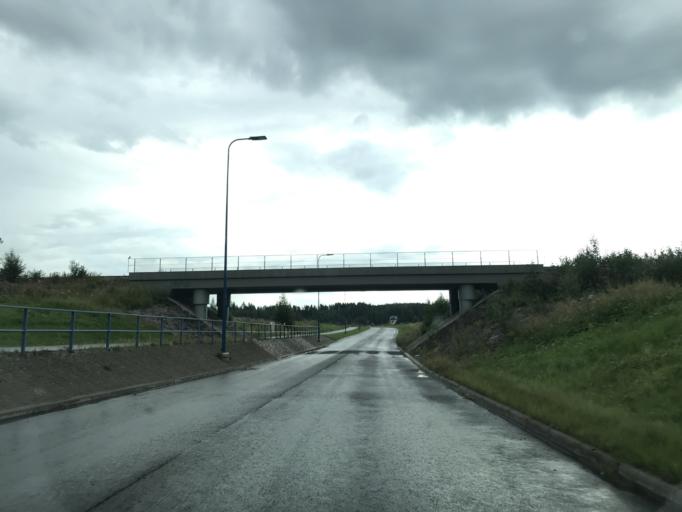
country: FI
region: Uusimaa
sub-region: Helsinki
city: Vihti
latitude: 60.3237
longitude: 24.3066
